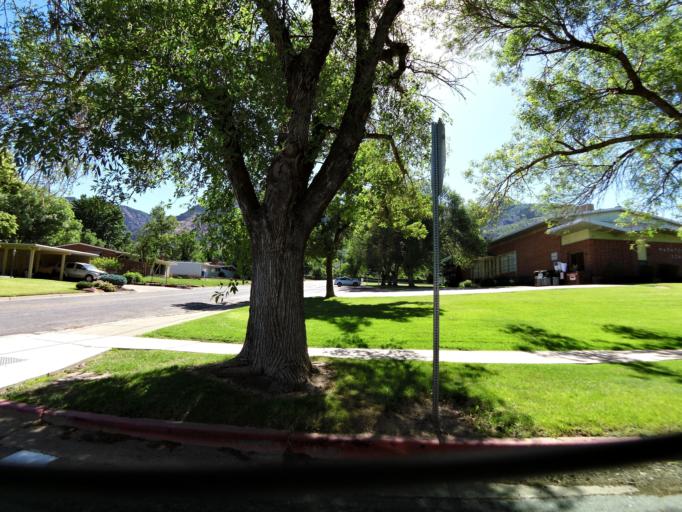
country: US
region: Utah
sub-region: Weber County
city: South Ogden
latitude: 41.2024
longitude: -111.9437
